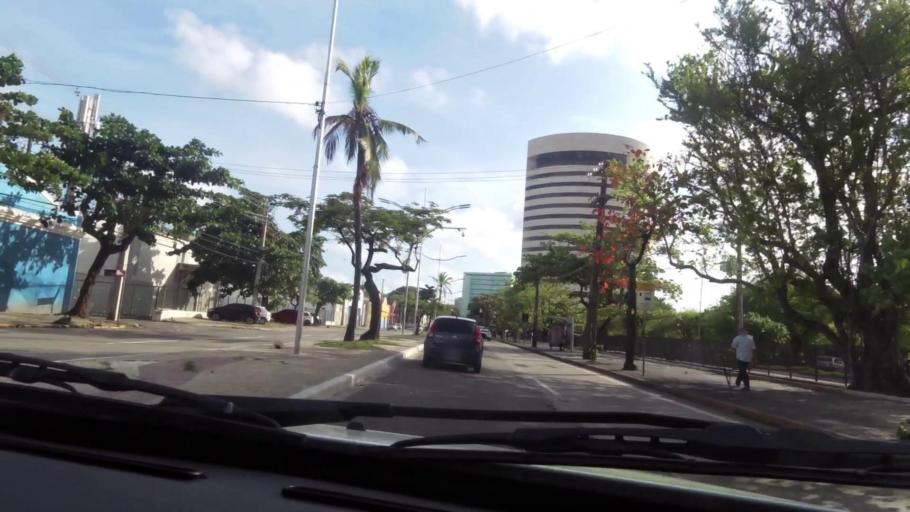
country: BR
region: Pernambuco
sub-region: Recife
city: Recife
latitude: -8.0590
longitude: -34.8727
